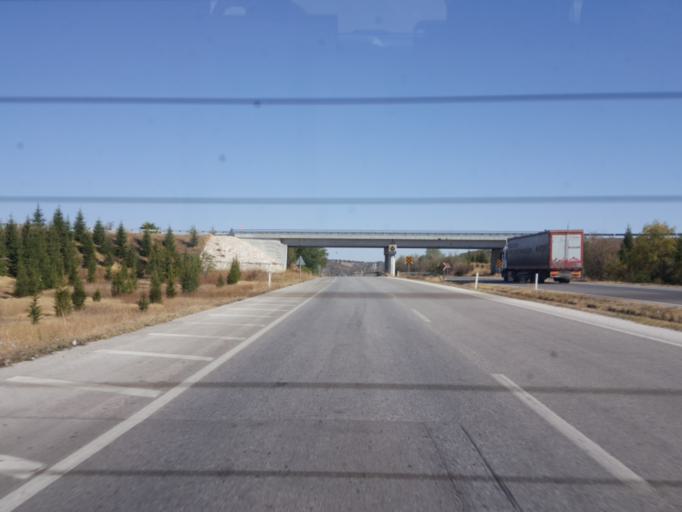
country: TR
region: Corum
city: Alaca
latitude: 40.2926
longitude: 34.6522
